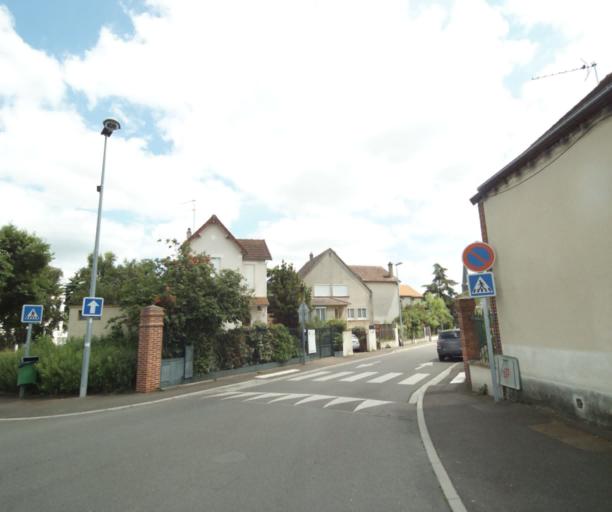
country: FR
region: Centre
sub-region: Departement d'Eure-et-Loir
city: Luce
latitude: 48.4408
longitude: 1.4654
